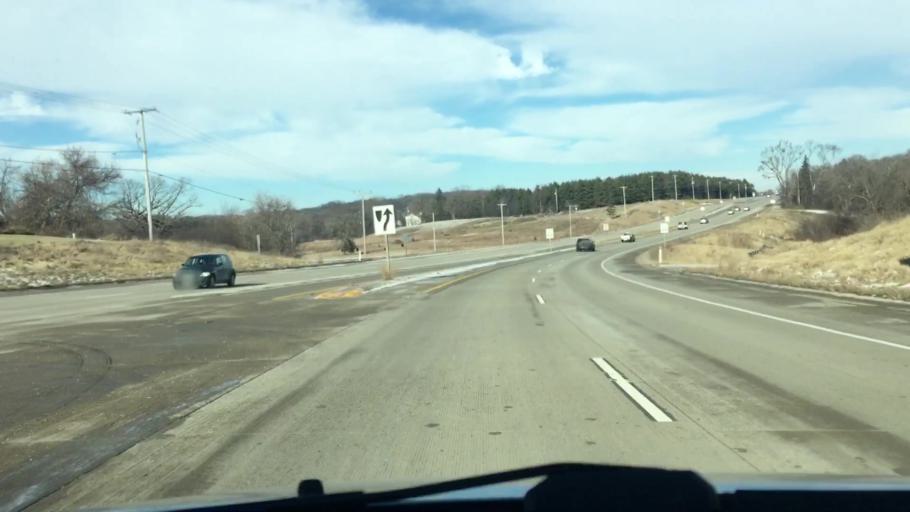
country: US
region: Wisconsin
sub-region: Waukesha County
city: Mukwonago
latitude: 42.8823
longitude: -88.3429
